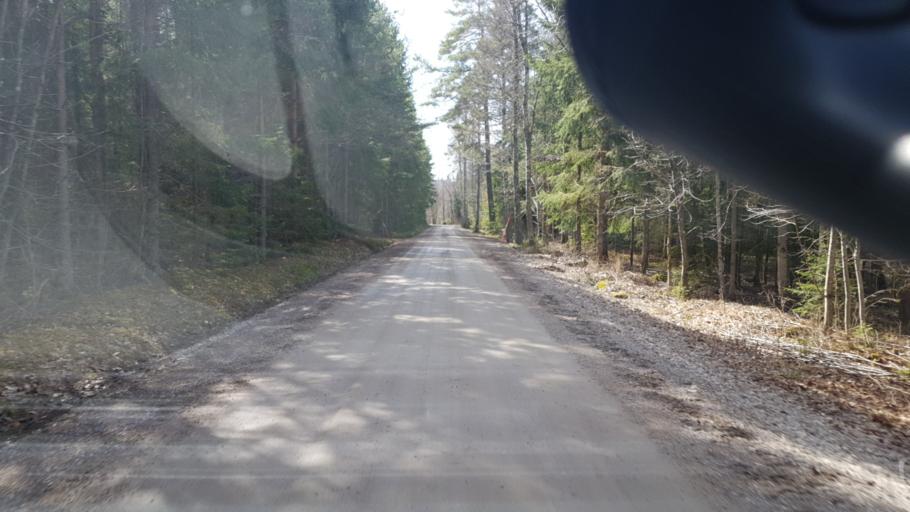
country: SE
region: Vaermland
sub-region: Arvika Kommun
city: Arvika
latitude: 59.5116
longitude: 12.7304
